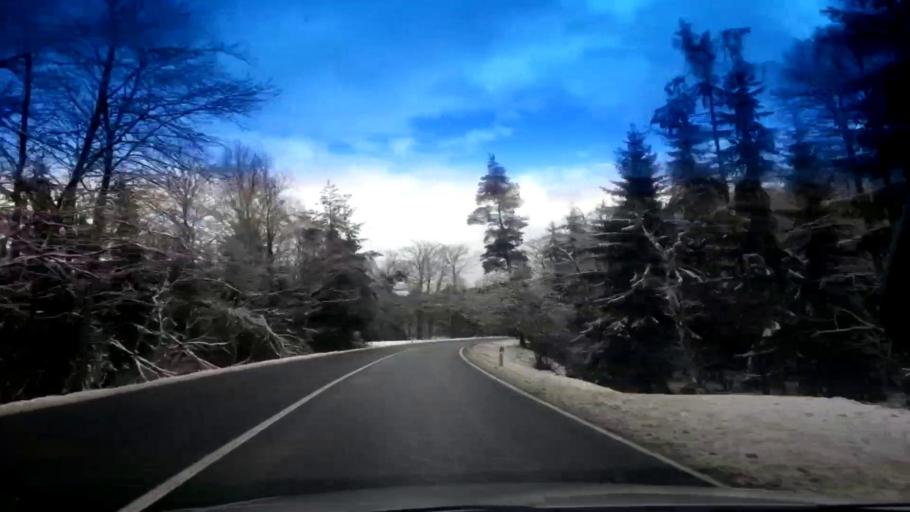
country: CZ
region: Karlovarsky
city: Hazlov
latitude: 50.1885
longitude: 12.2378
